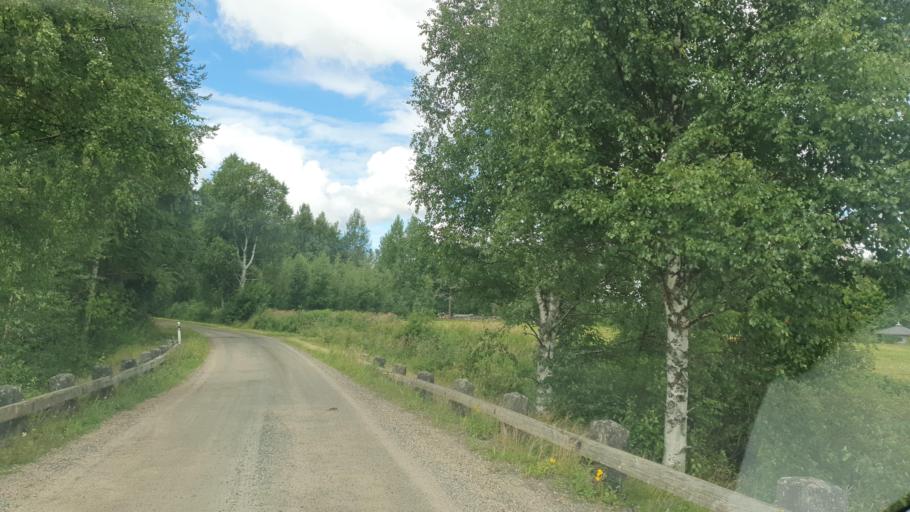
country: FI
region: Kainuu
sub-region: Kehys-Kainuu
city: Kuhmo
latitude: 64.0874
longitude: 29.0963
